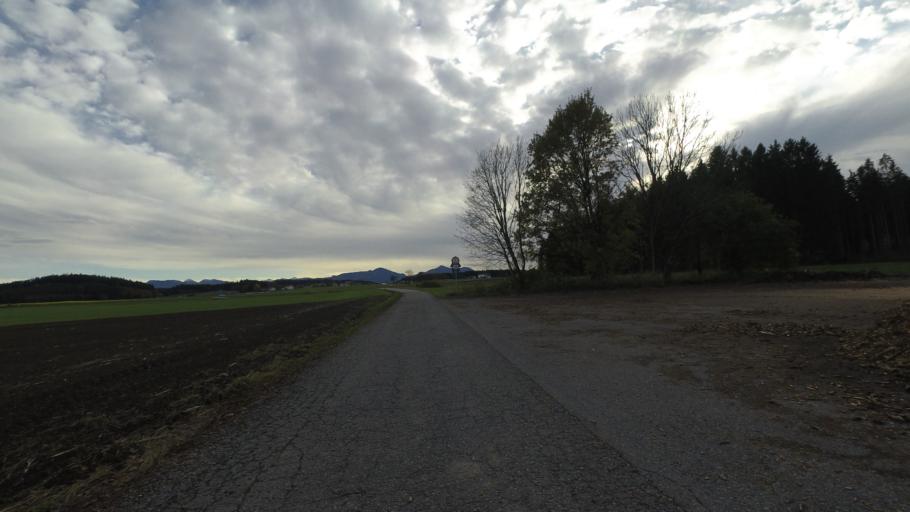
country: DE
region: Bavaria
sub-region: Upper Bavaria
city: Nussdorf
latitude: 47.9329
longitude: 12.5921
